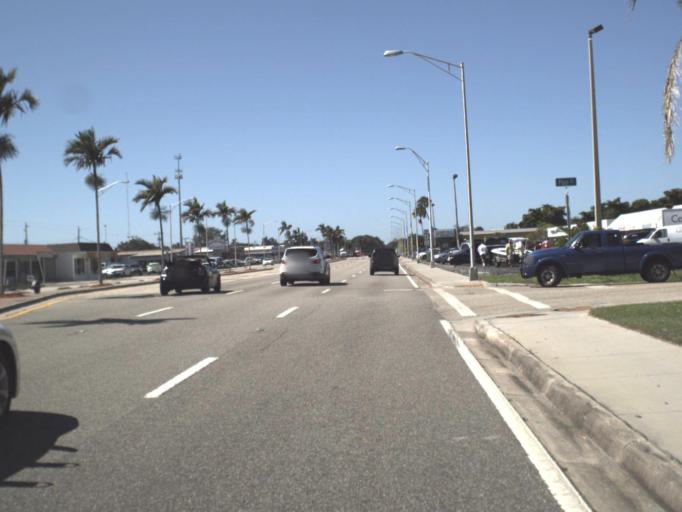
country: US
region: Florida
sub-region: Collier County
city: Naples
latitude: 26.1385
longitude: -81.7745
